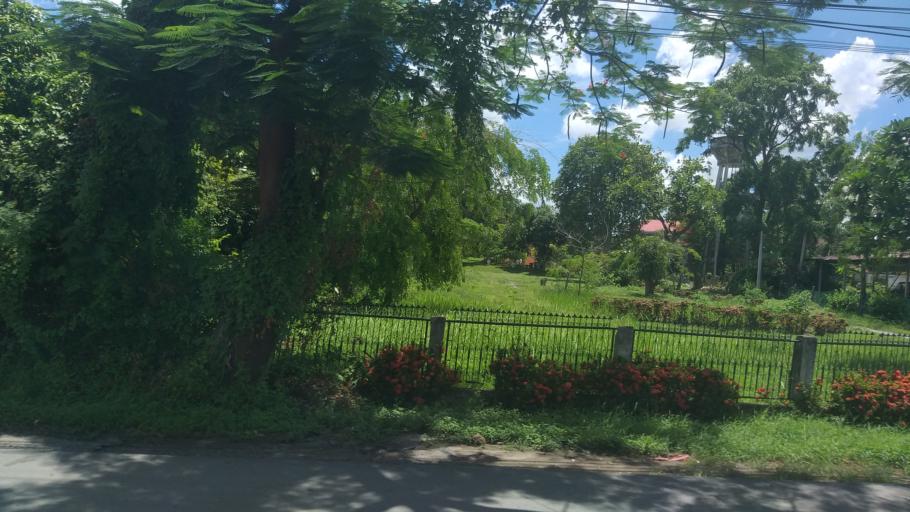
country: TH
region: Nakhon Nayok
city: Ban Na
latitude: 14.2905
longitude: 101.0676
